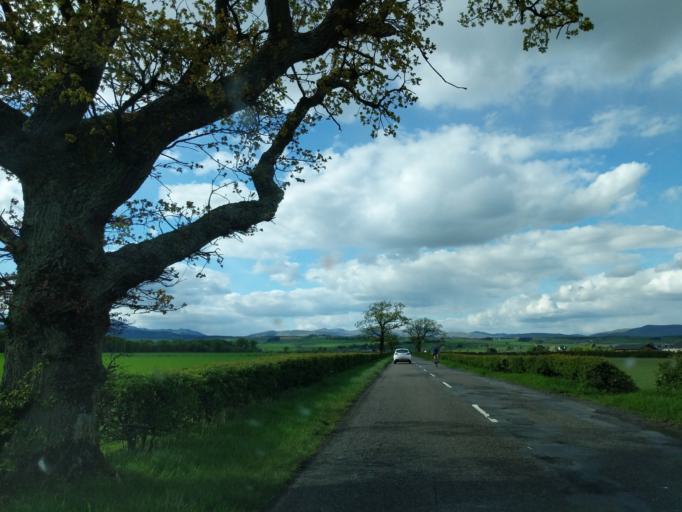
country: GB
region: Scotland
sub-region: Stirling
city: Callander
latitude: 56.1534
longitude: -4.1632
